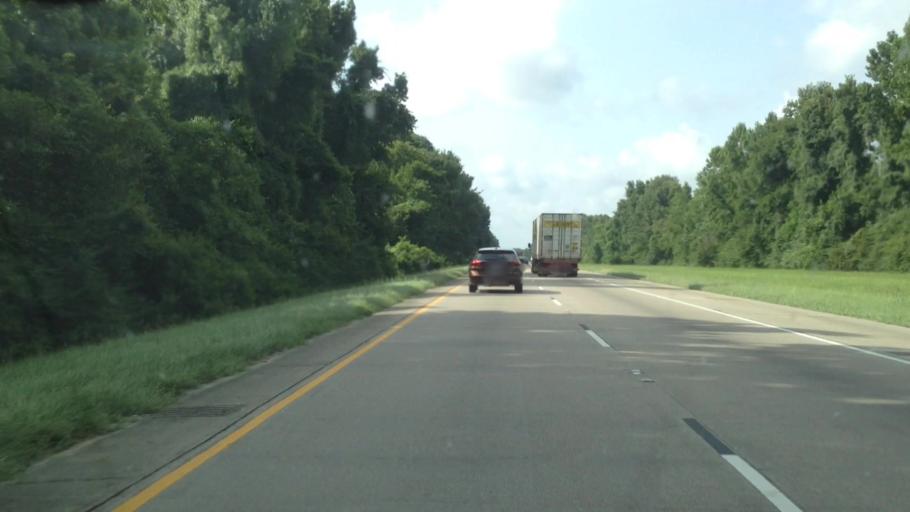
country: US
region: Louisiana
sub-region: Ascension Parish
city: Prairieville
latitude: 30.2974
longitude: -90.9923
